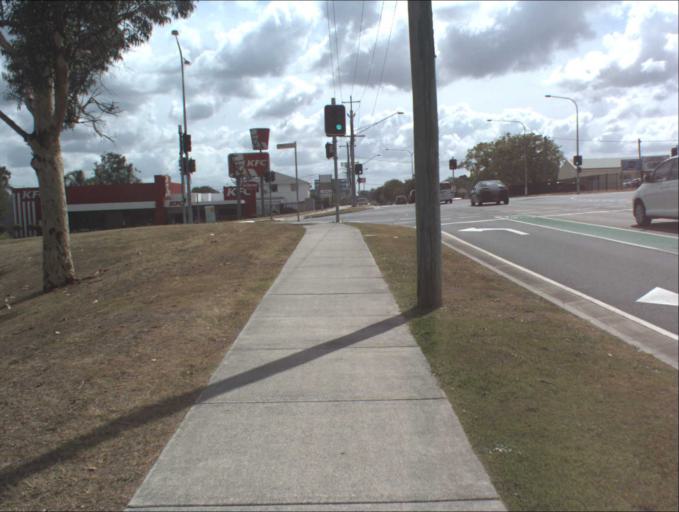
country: AU
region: Queensland
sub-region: Logan
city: Beenleigh
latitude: -27.7193
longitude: 153.1975
